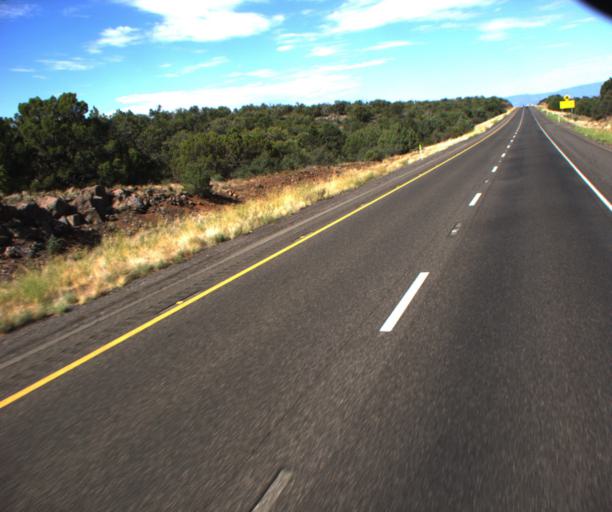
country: US
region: Arizona
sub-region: Yavapai County
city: Village of Oak Creek (Big Park)
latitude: 34.7798
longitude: -111.6235
